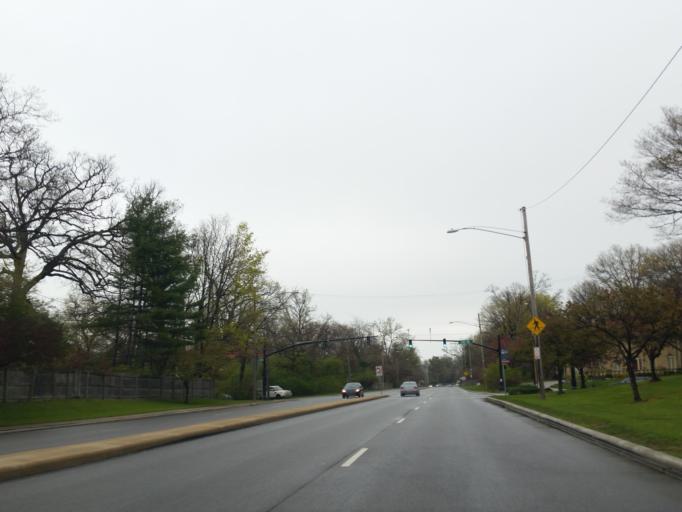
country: US
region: Ohio
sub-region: Cuyahoga County
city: Rocky River
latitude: 41.4870
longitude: -81.8311
